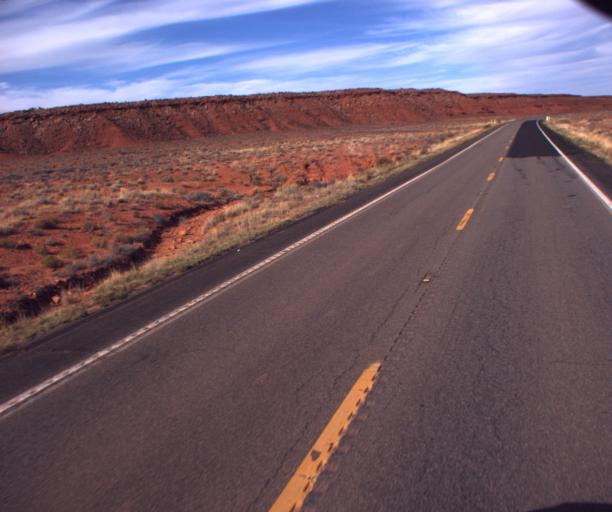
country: US
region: Arizona
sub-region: Navajo County
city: Kayenta
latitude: 36.9020
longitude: -109.7901
